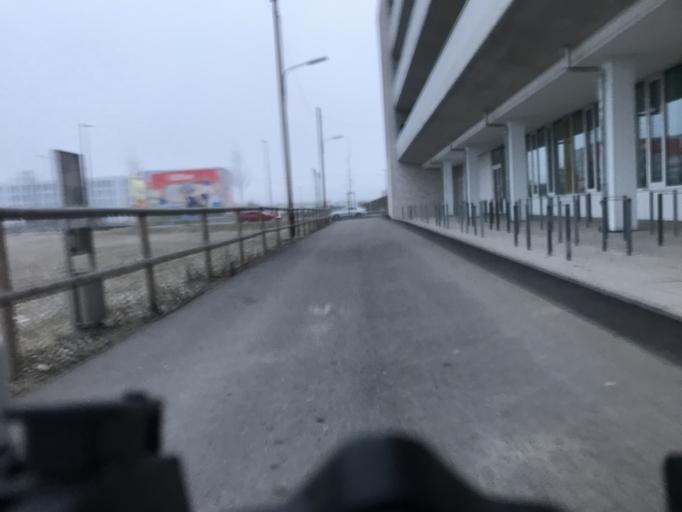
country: DE
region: Bavaria
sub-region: Upper Bavaria
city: Germering
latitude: 48.1411
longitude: 11.4071
